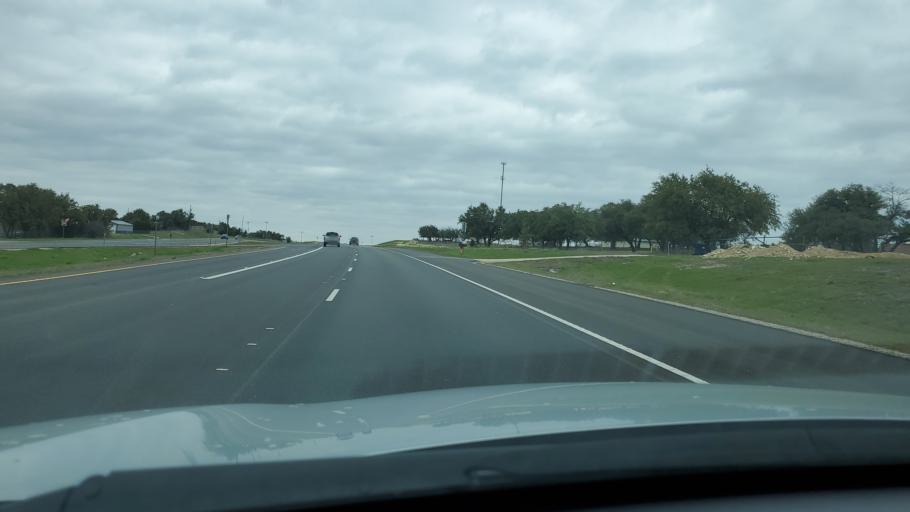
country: US
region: Texas
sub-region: Williamson County
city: Florence
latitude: 30.9292
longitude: -97.7924
